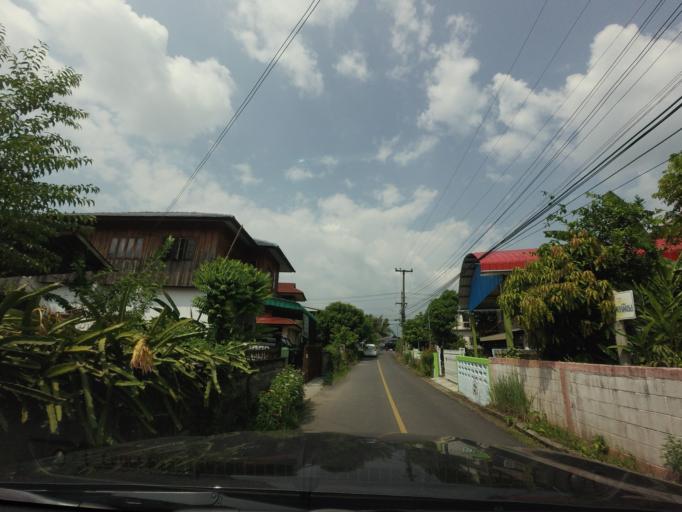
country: TH
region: Nan
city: Pua
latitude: 19.1743
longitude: 100.9377
